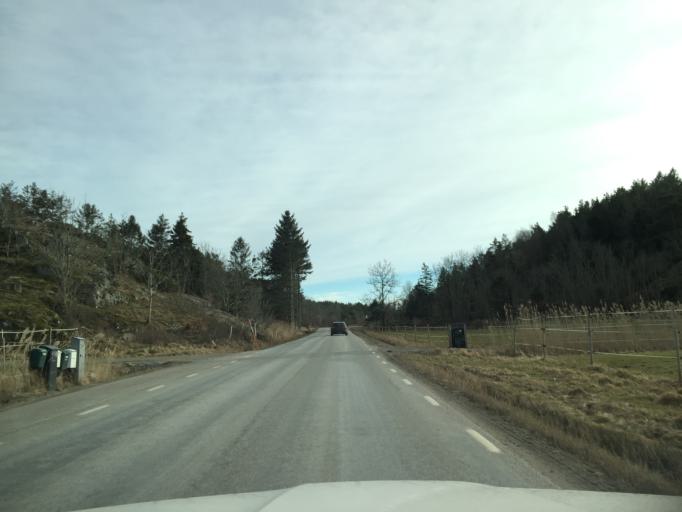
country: SE
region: Vaestra Goetaland
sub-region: Tjorns Kommun
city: Skaerhamn
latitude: 58.0340
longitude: 11.5915
